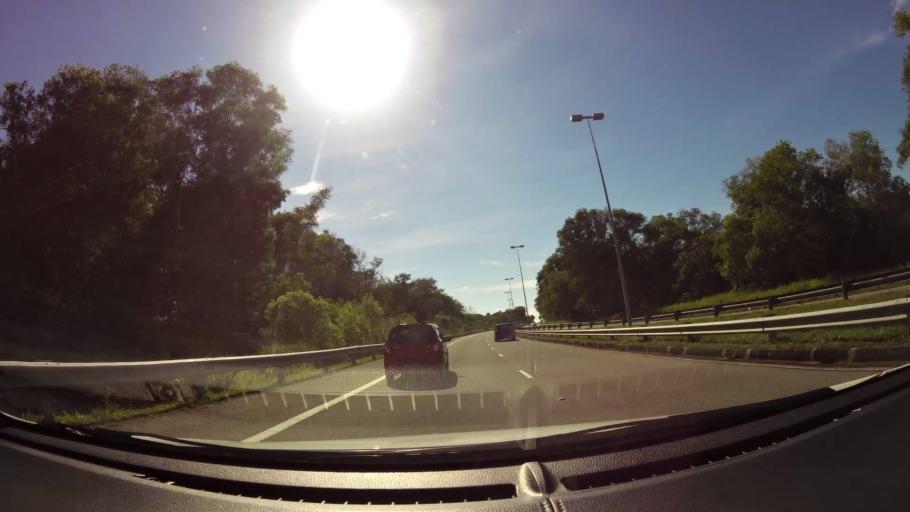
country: BN
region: Brunei and Muara
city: Bandar Seri Begawan
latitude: 4.9827
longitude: 114.9313
